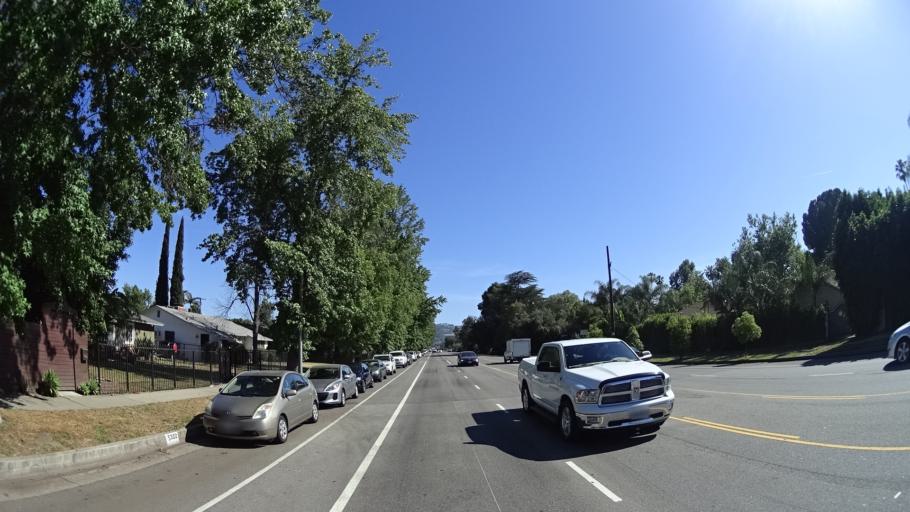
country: US
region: California
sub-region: Los Angeles County
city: Sherman Oaks
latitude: 34.1673
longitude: -118.4314
